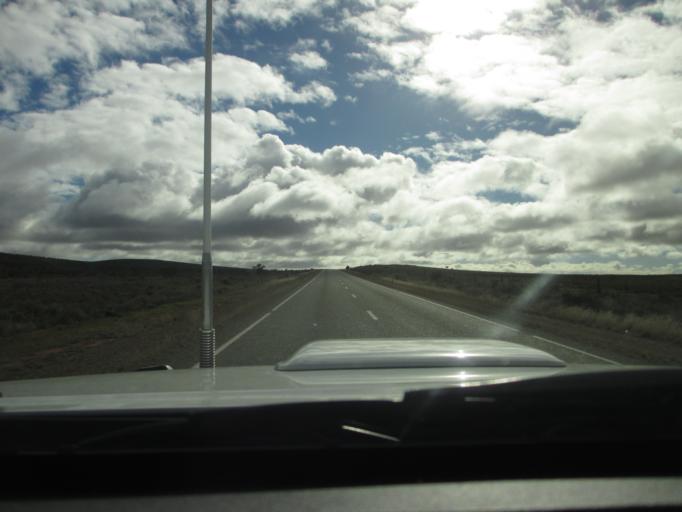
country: AU
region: South Australia
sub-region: Flinders Ranges
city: Quorn
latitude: -32.1896
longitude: 138.5352
